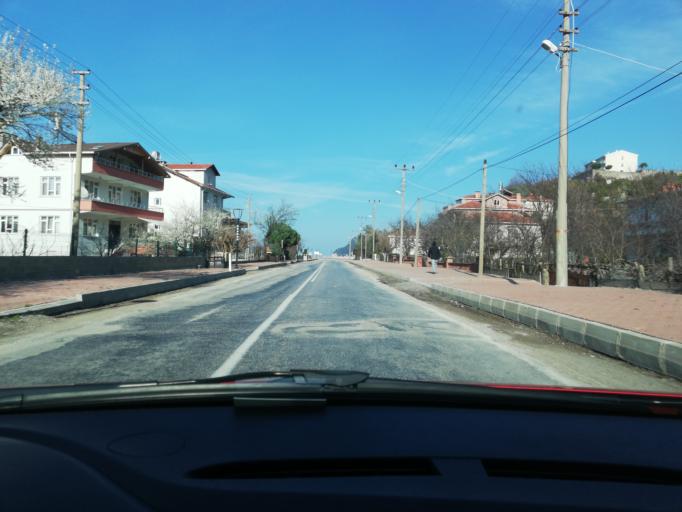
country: TR
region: Kastamonu
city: Cide
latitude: 41.8816
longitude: 32.9445
